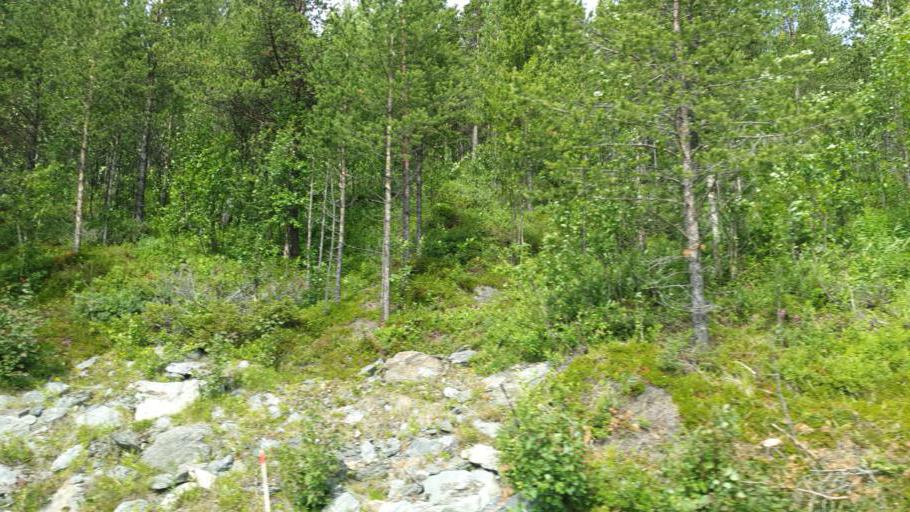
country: NO
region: Oppland
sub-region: Vaga
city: Vagamo
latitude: 61.6764
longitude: 9.0451
